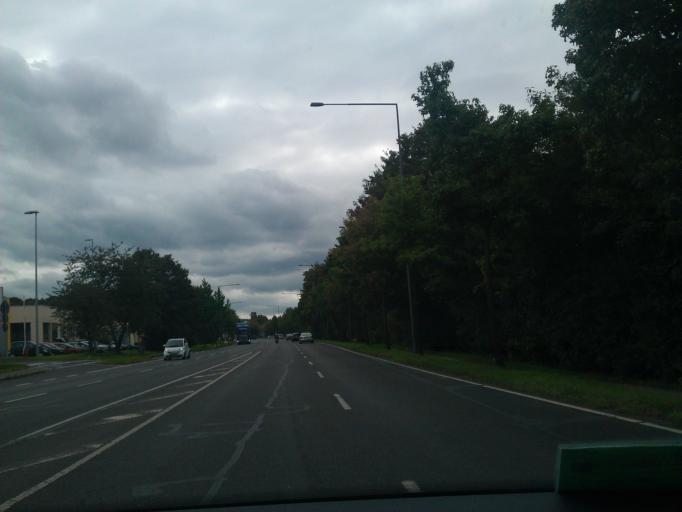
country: DE
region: North Rhine-Westphalia
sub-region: Regierungsbezirk Koln
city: Aachen
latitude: 50.7803
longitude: 6.1218
